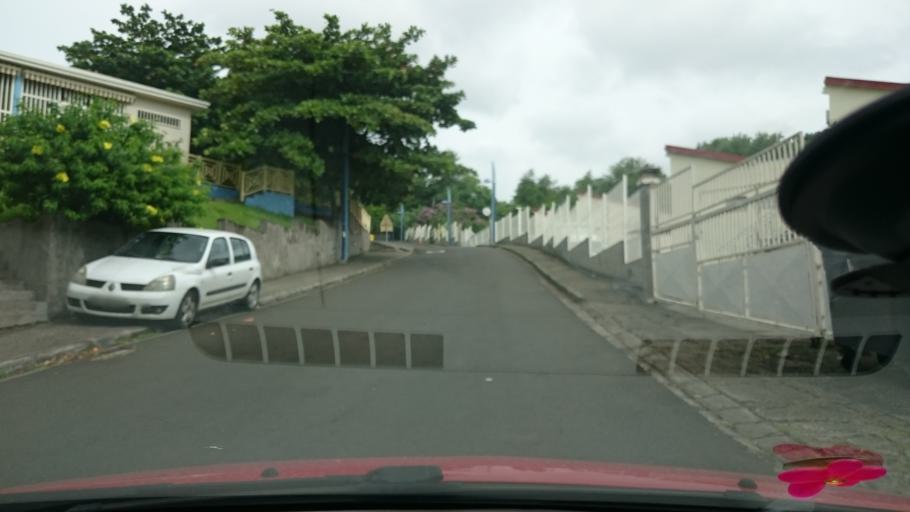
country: MQ
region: Martinique
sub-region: Martinique
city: Riviere-Pilote
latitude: 14.4827
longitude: -60.9060
